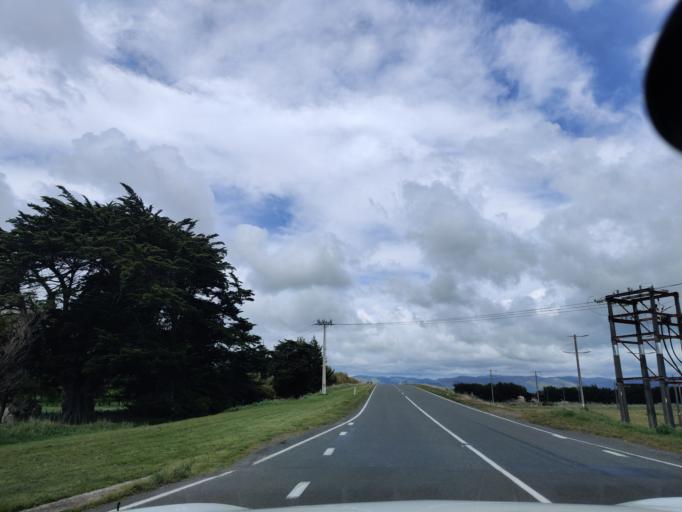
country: NZ
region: Manawatu-Wanganui
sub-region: Palmerston North City
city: Palmerston North
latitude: -40.3656
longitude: 175.5519
